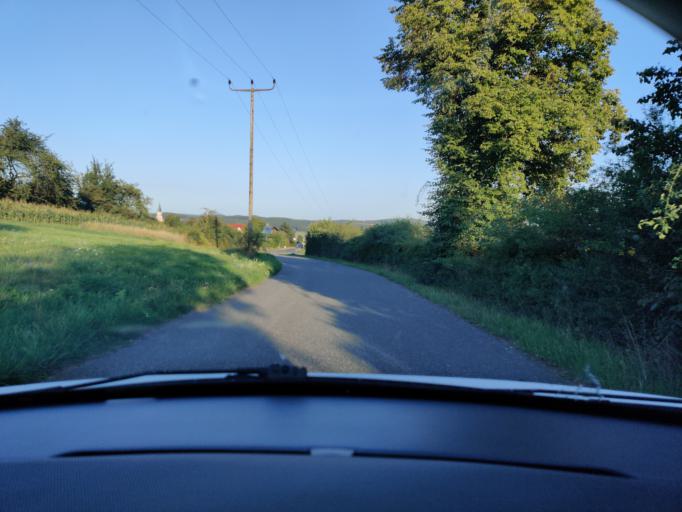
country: DE
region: Bavaria
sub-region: Upper Palatinate
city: Nabburg
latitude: 49.4559
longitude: 12.1680
